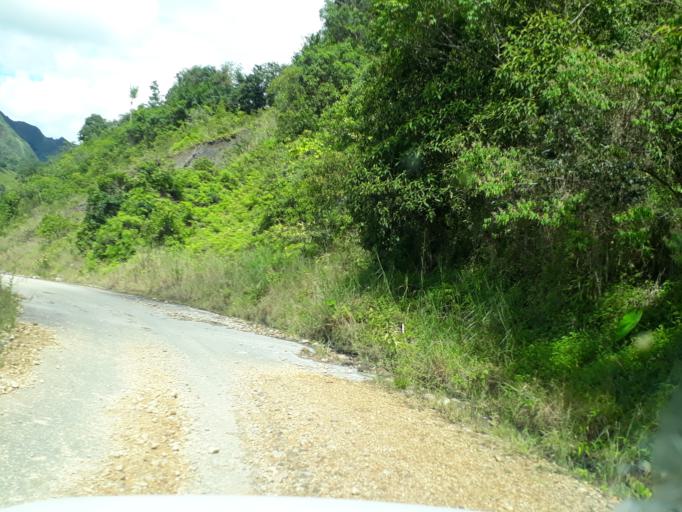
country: CO
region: Cundinamarca
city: Medina
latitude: 4.6380
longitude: -73.3114
